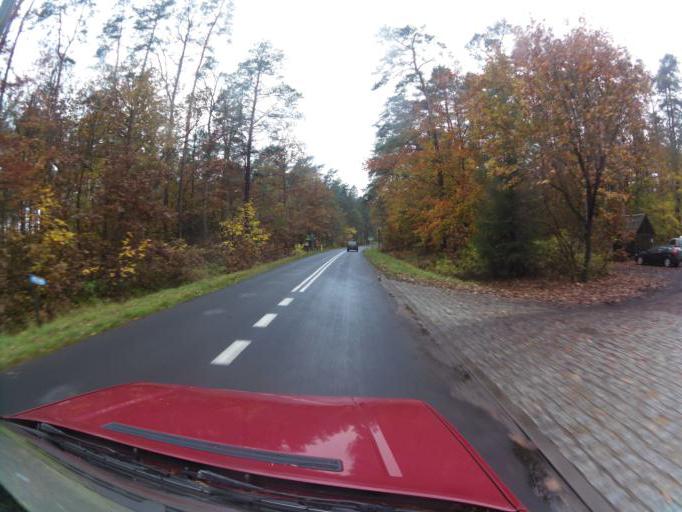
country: PL
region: West Pomeranian Voivodeship
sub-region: Powiat policki
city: Dobra
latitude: 53.5848
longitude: 14.3839
